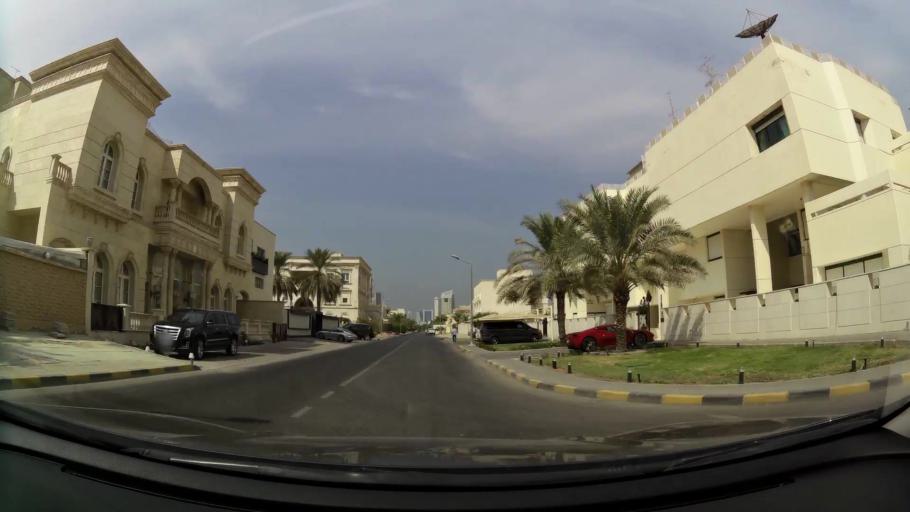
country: KW
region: Al Asimah
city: Ad Dasmah
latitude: 29.3520
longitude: 47.9905
